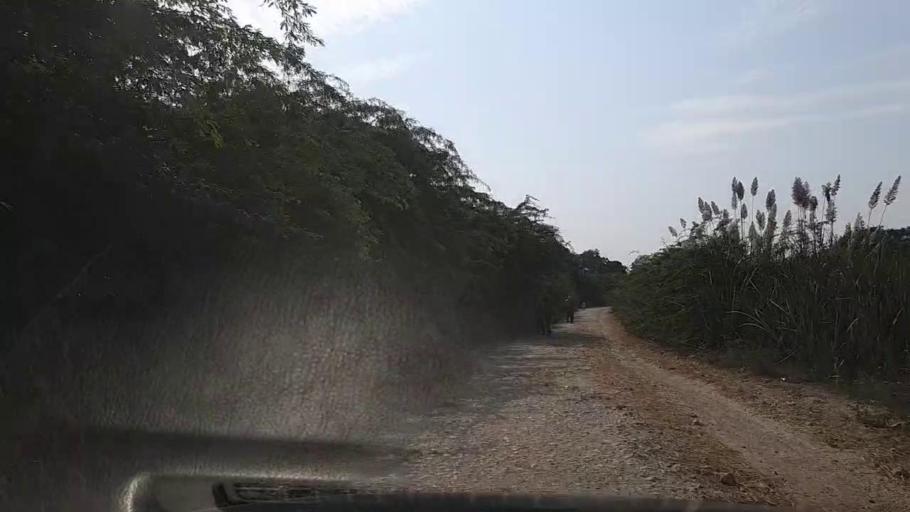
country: PK
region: Sindh
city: Thatta
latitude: 24.7493
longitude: 67.7739
